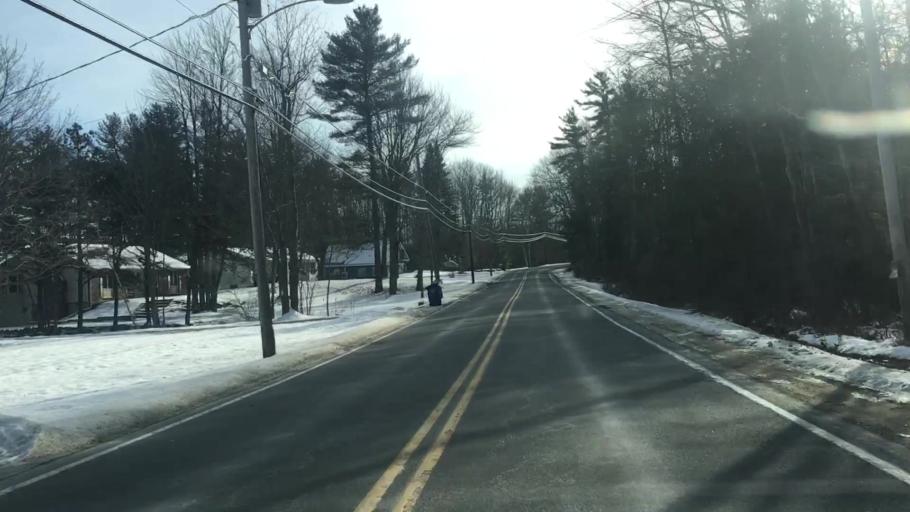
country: US
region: Maine
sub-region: Cumberland County
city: Westbrook
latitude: 43.7087
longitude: -70.3580
